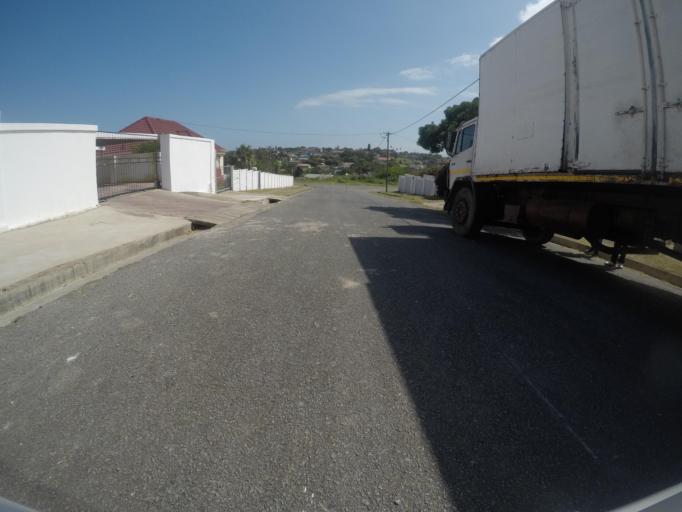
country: ZA
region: Eastern Cape
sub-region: Buffalo City Metropolitan Municipality
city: East London
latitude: -32.9780
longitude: 27.8691
